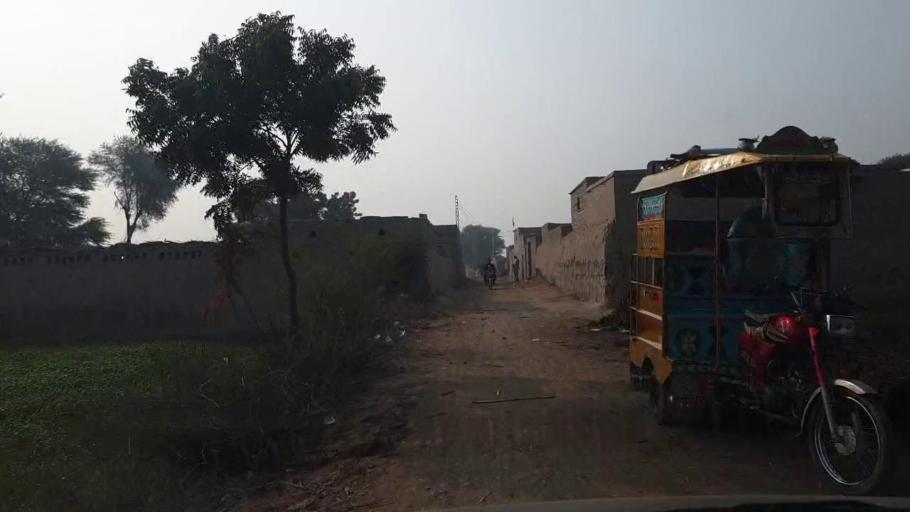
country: PK
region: Sindh
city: Hala
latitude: 25.8720
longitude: 68.3932
